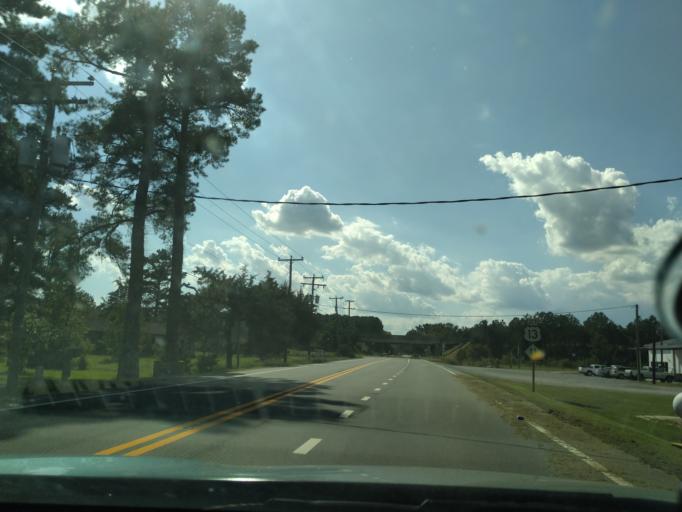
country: US
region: North Carolina
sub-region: Pitt County
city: Bethel
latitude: 35.8085
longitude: -77.3636
